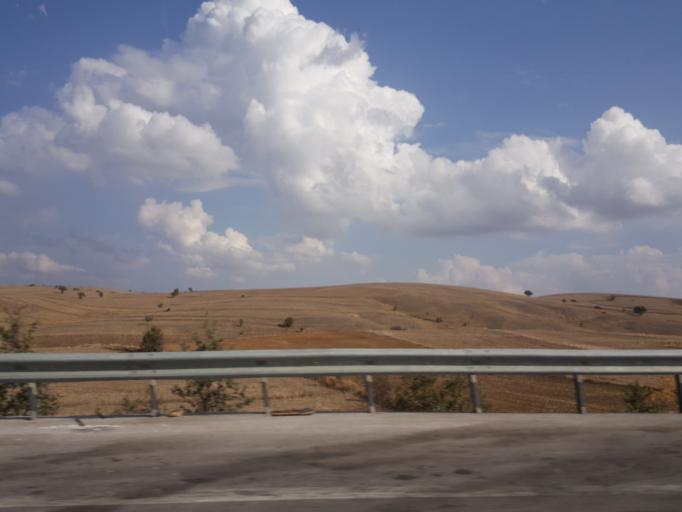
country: TR
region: Corum
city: Alaca
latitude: 40.2961
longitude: 34.6537
